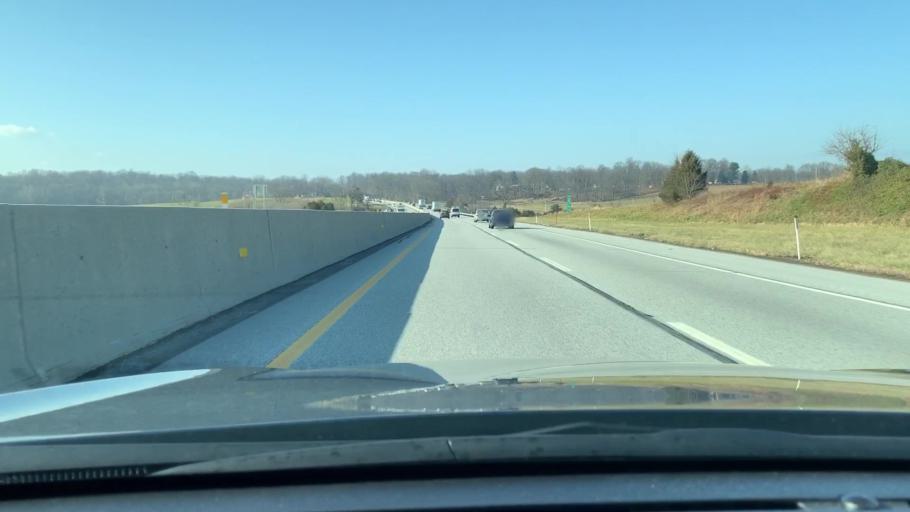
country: US
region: Pennsylvania
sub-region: Lancaster County
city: Elizabethtown
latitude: 40.2084
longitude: -76.6090
